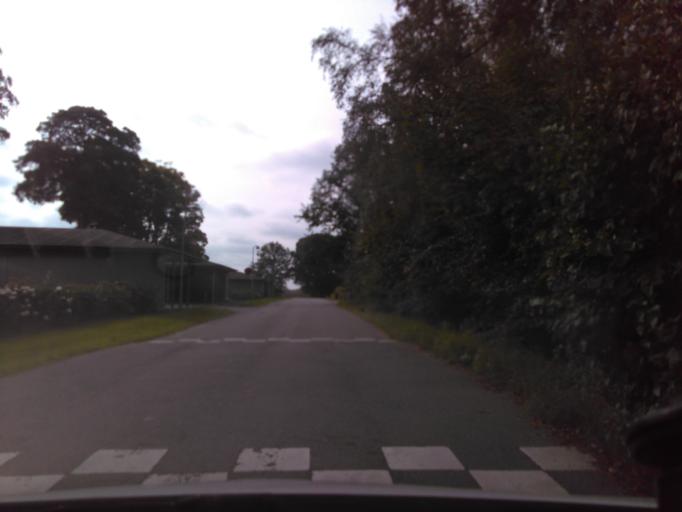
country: DK
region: Capital Region
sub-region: Ballerup Kommune
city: Malov
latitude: 55.7753
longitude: 12.3179
